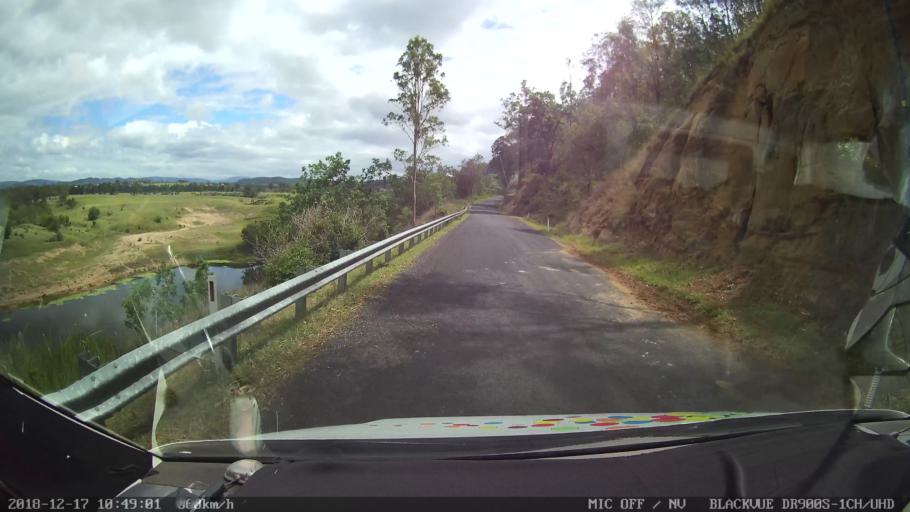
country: AU
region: New South Wales
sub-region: Clarence Valley
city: Gordon
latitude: -28.8689
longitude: 152.5719
